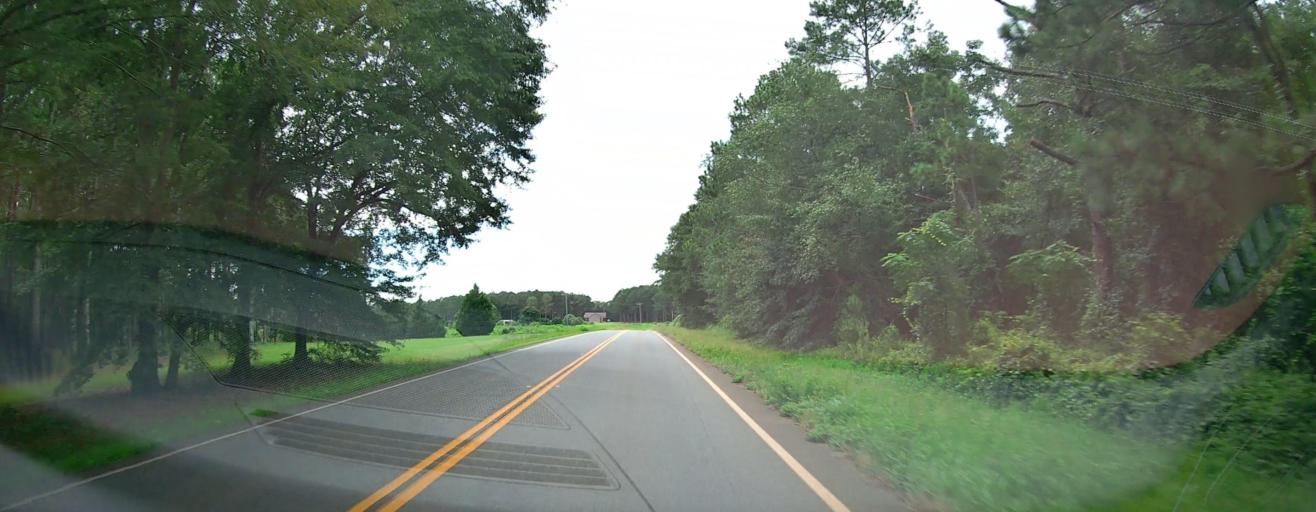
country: US
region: Georgia
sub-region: Schley County
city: Ellaville
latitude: 32.2525
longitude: -84.3960
